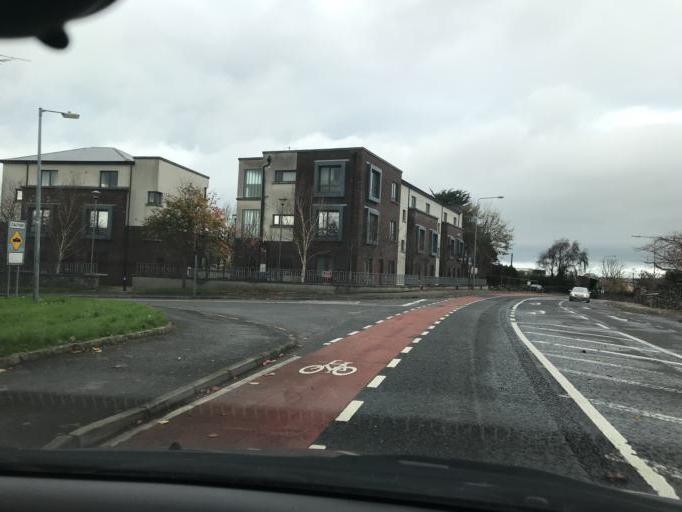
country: IE
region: Connaught
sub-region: Sligo
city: Sligo
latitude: 54.2739
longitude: -8.5040
